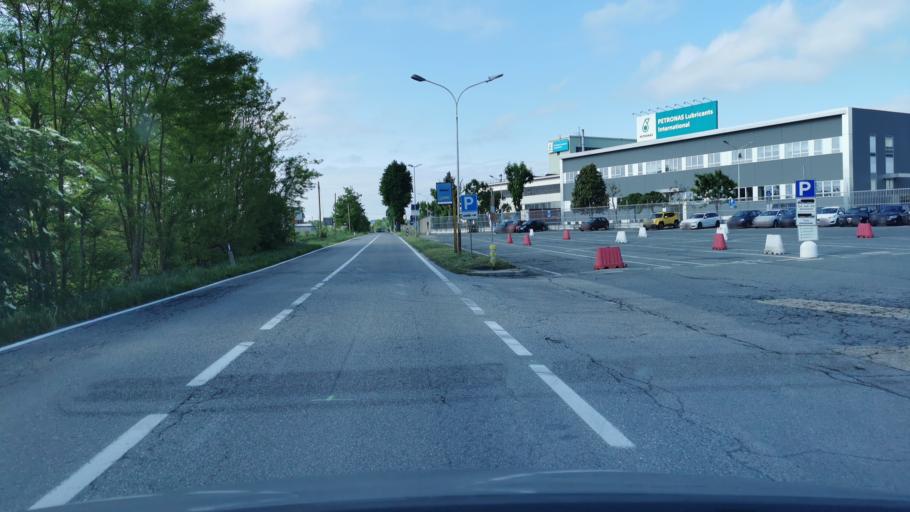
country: IT
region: Piedmont
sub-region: Provincia di Torino
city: Villastellone
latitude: 44.9330
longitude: 7.7572
